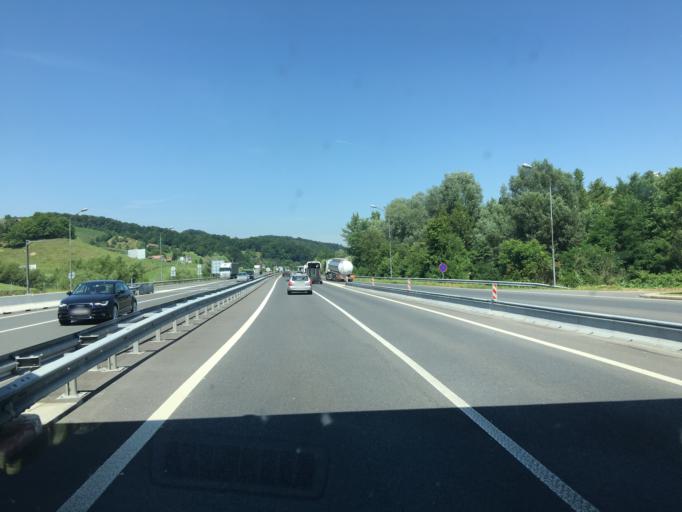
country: SI
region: Pesnica
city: Pesnica pri Mariboru
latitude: 46.6147
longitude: 15.6618
